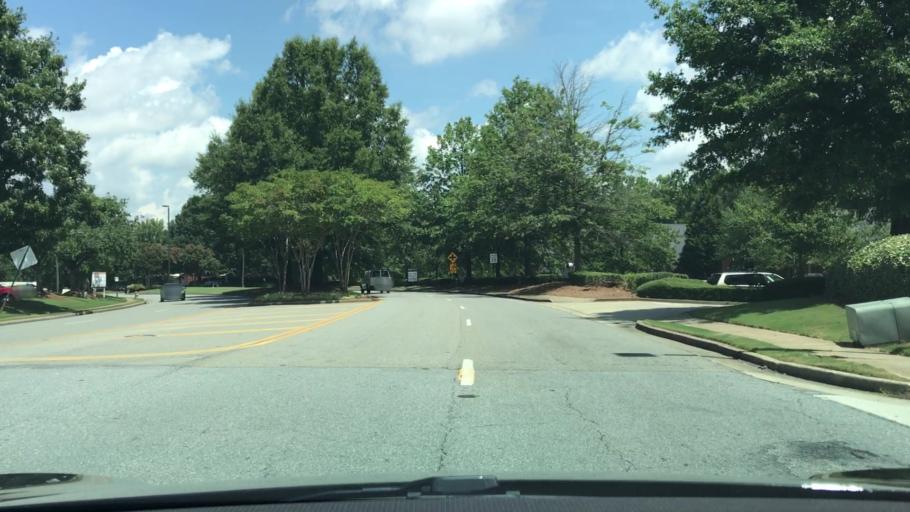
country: US
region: Georgia
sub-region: Fulton County
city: Johns Creek
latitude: 34.0670
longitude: -84.1623
